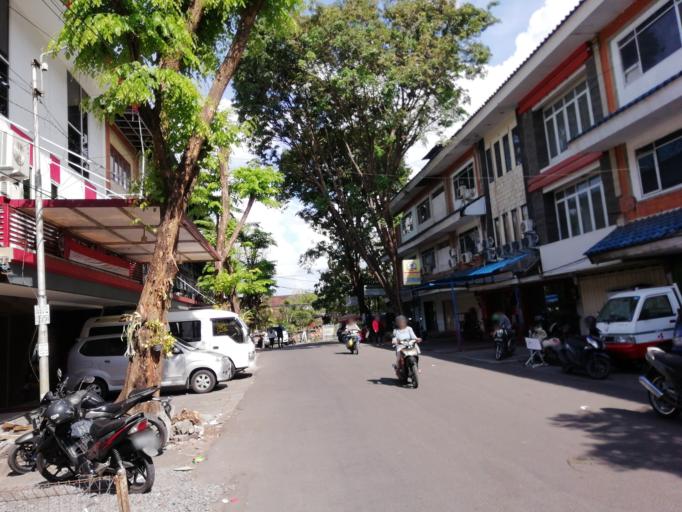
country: ID
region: Bali
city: Denpasar
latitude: -8.6703
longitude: 115.2141
